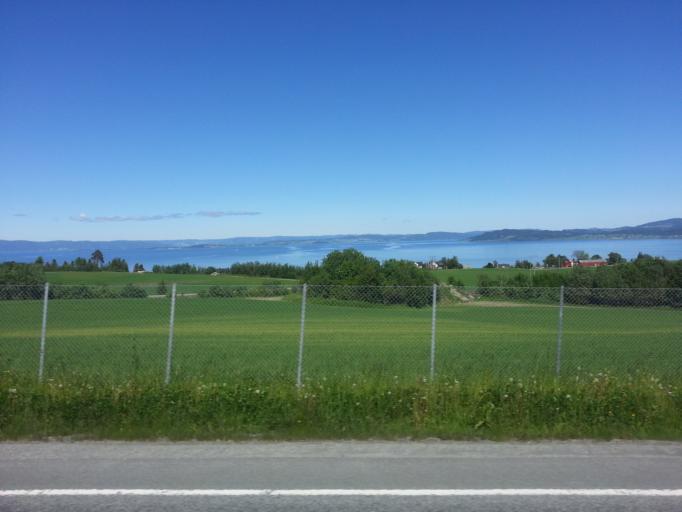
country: NO
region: Sor-Trondelag
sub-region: Malvik
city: Malvik
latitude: 63.4258
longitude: 10.6773
